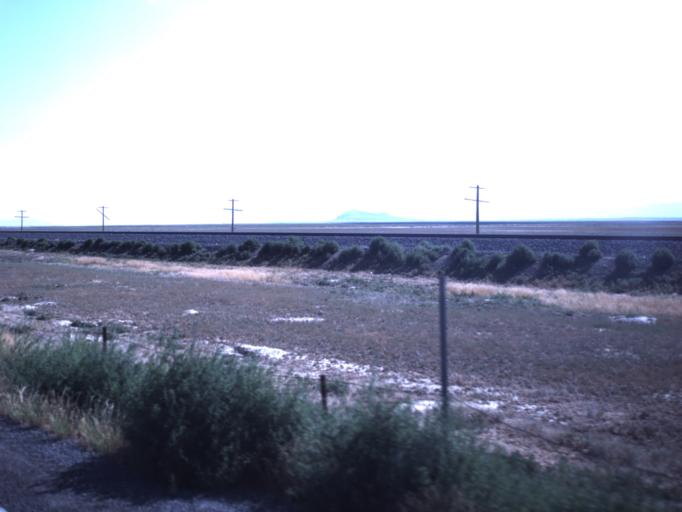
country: US
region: Utah
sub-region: Millard County
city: Delta
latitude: 39.0066
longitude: -112.7849
